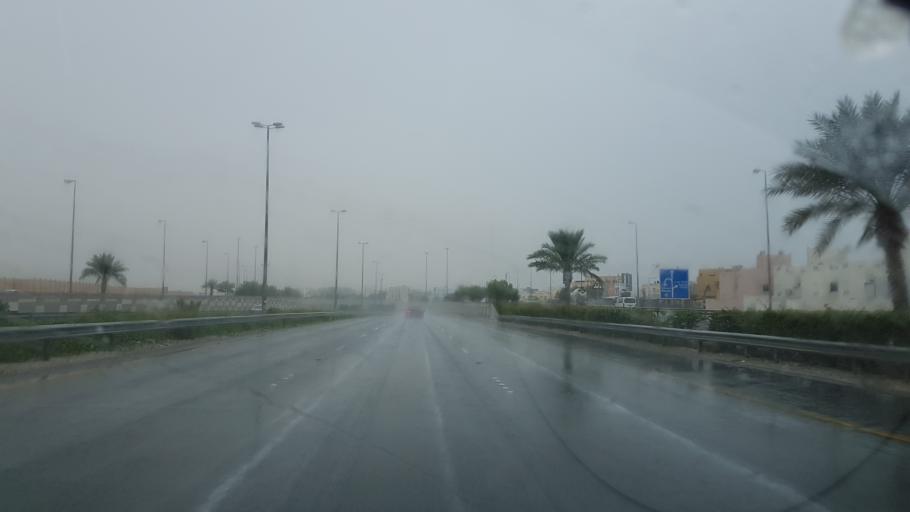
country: BH
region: Central Governorate
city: Madinat Hamad
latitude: 26.1021
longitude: 50.5112
